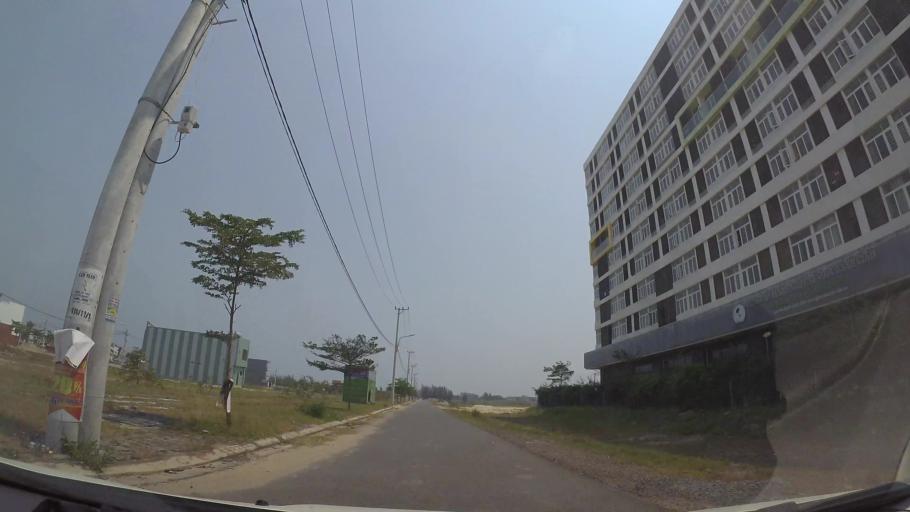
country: VN
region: Da Nang
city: Ngu Hanh Son
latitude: 15.9841
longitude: 108.2610
